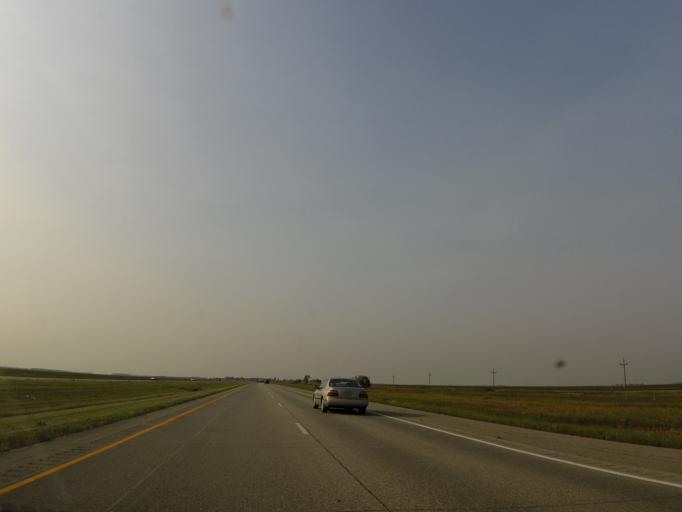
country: US
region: North Dakota
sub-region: Cass County
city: West Fargo
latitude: 47.0289
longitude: -96.9173
